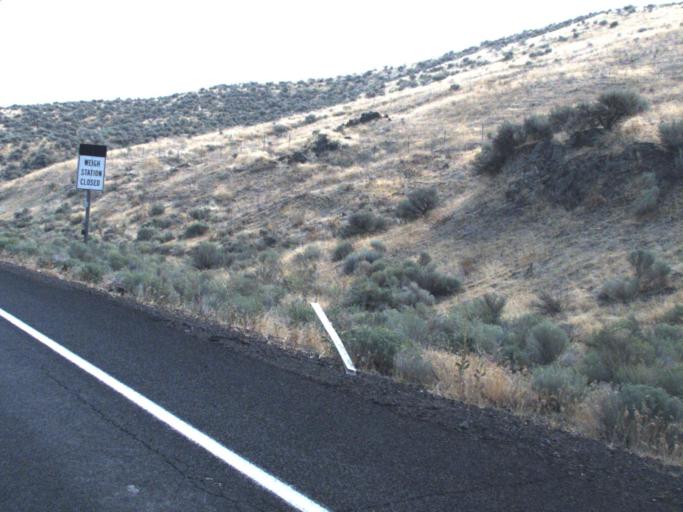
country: US
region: Washington
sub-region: Yakima County
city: Toppenish
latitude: 46.3031
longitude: -120.3396
